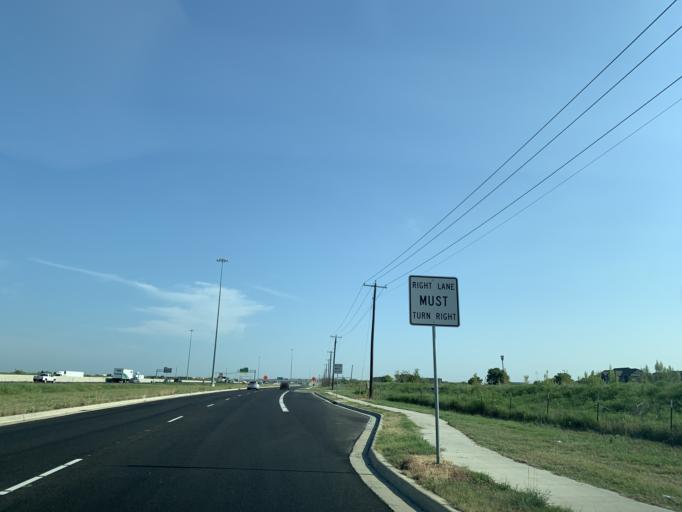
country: US
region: Texas
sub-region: Tarrant County
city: Blue Mound
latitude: 32.8888
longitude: -97.3164
